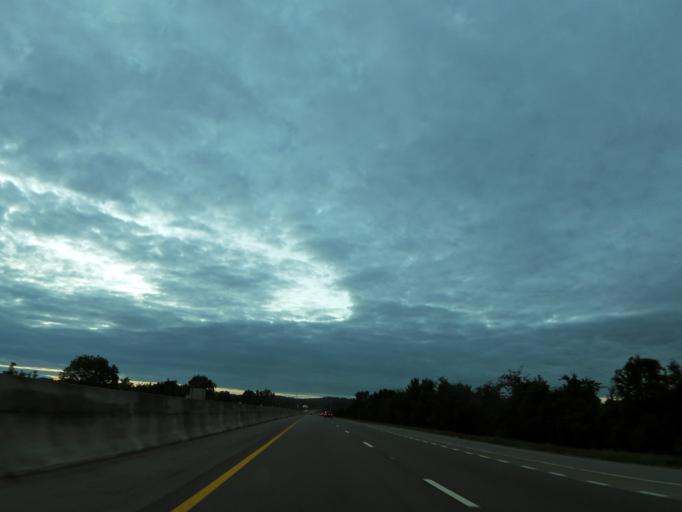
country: US
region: Tennessee
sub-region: Davidson County
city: Nashville
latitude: 36.1923
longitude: -86.8645
